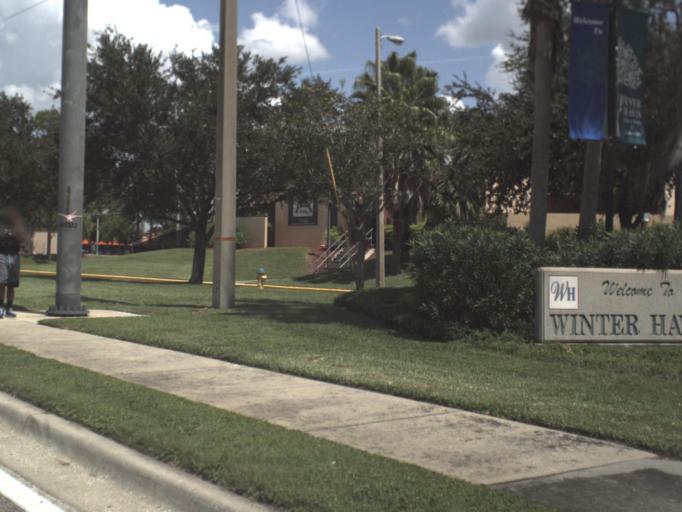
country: US
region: Florida
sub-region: Polk County
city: Winter Haven
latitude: 28.0027
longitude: -81.7311
